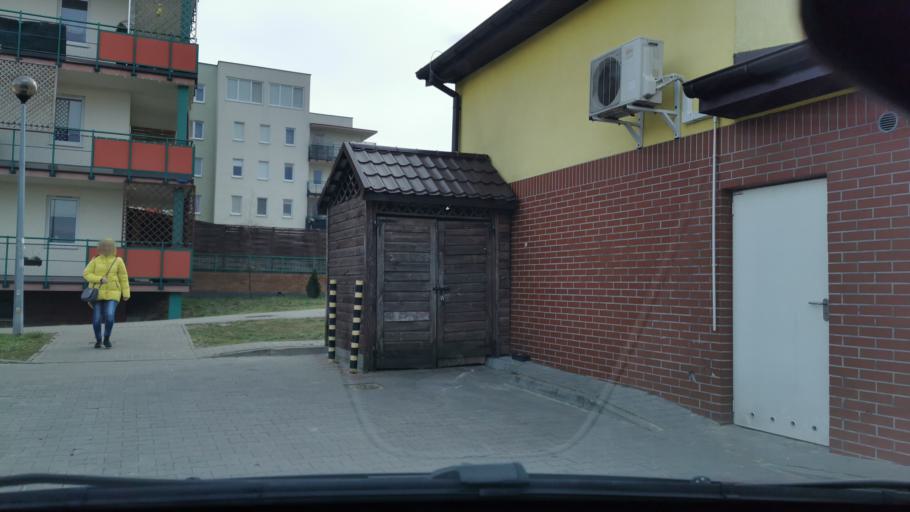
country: PL
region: Lublin Voivodeship
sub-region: Powiat lubelski
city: Lublin
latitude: 51.1987
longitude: 22.5423
